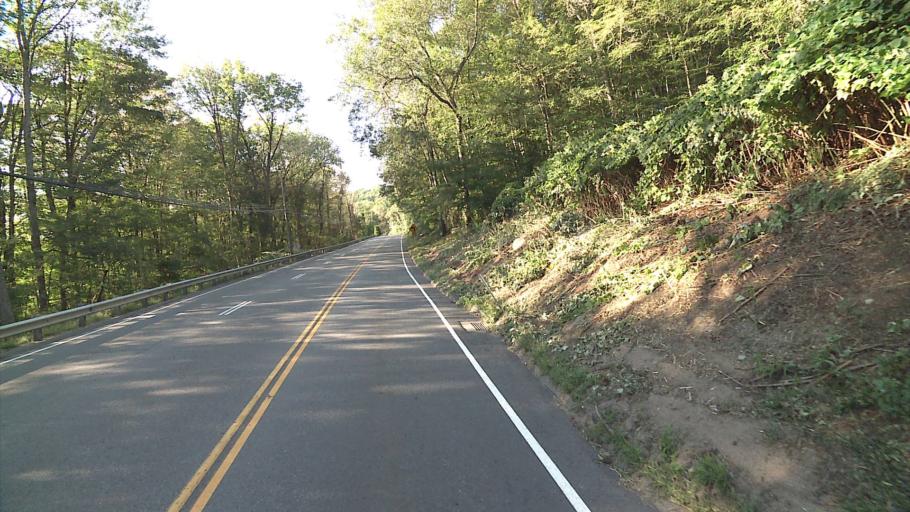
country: US
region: Connecticut
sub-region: New London County
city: Baltic
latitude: 41.6139
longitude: -72.1451
